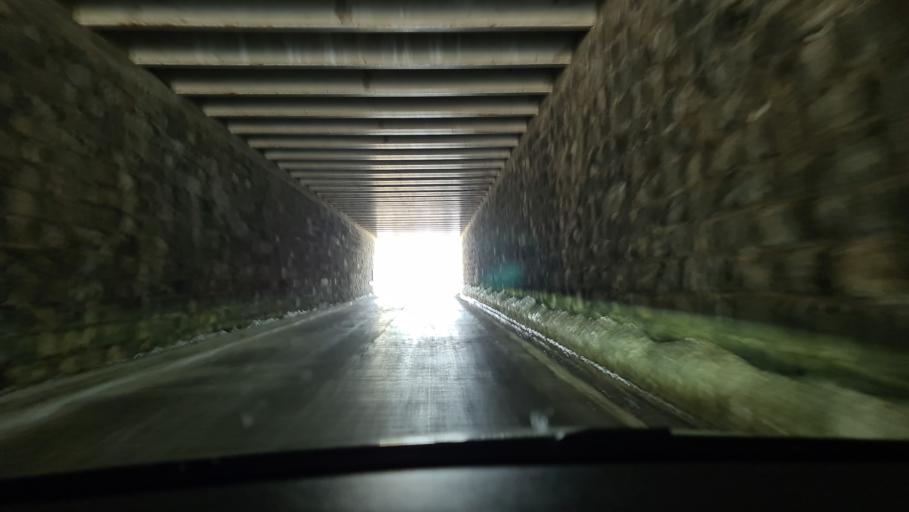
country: CH
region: Ticino
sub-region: Leventina District
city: Faido
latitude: 46.5508
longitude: 8.8105
